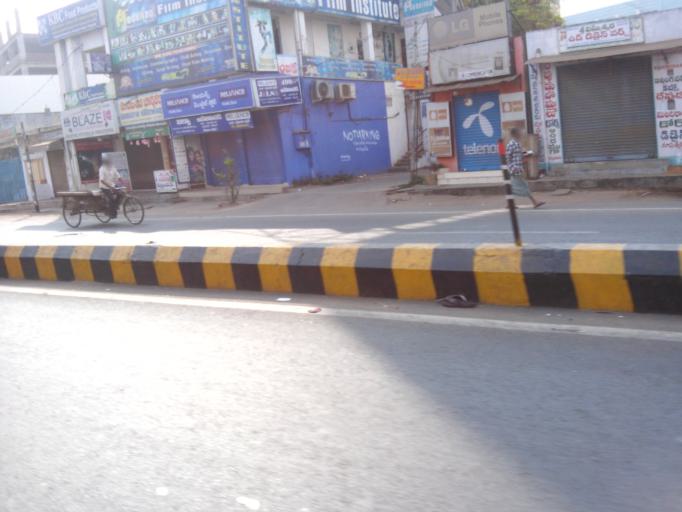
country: IN
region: Andhra Pradesh
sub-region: Krishna
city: Vijayawada
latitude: 16.5155
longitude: 80.6376
